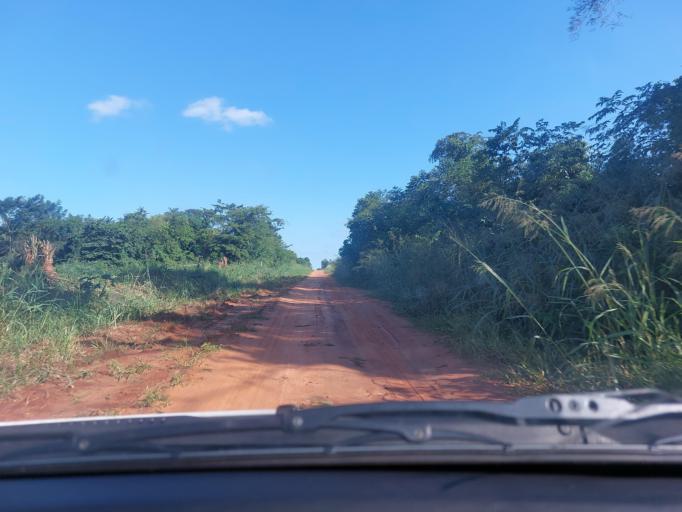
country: PY
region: San Pedro
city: Guayaybi
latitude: -24.5092
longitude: -56.5461
